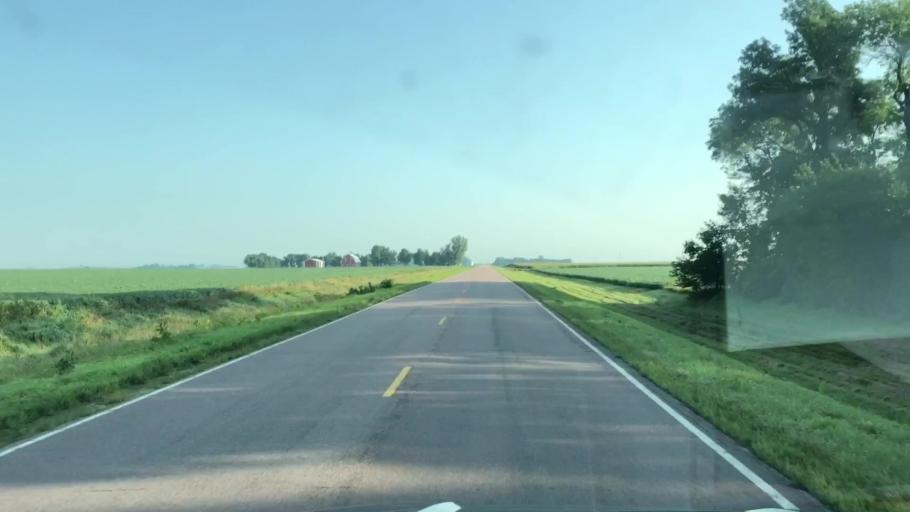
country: US
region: Iowa
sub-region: Lyon County
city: George
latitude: 43.3060
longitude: -95.9992
